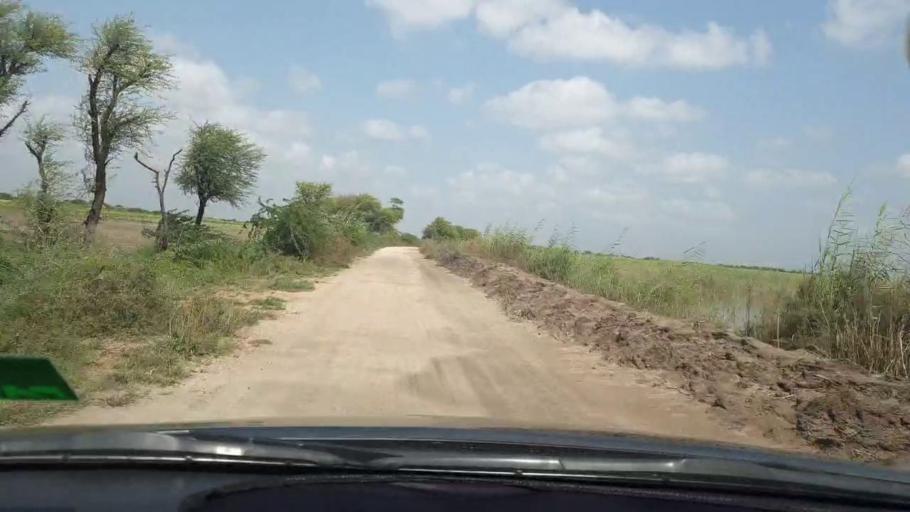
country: PK
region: Sindh
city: Tando Bago
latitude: 24.8563
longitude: 69.0356
